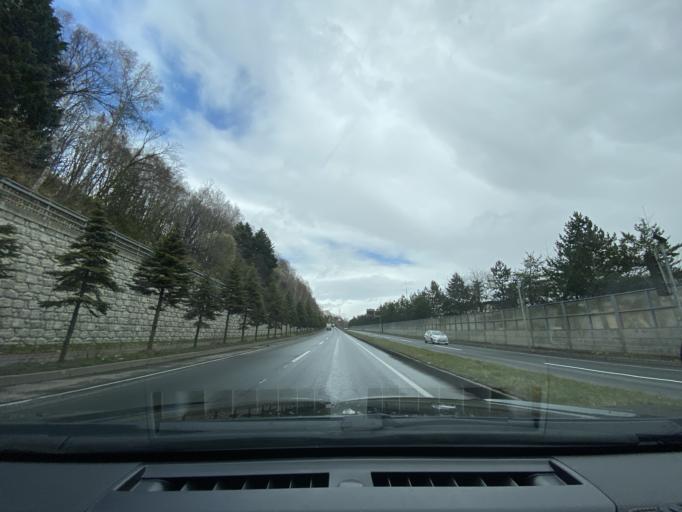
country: JP
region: Hokkaido
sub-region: Asahikawa-shi
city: Asahikawa
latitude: 43.8094
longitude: 142.3607
